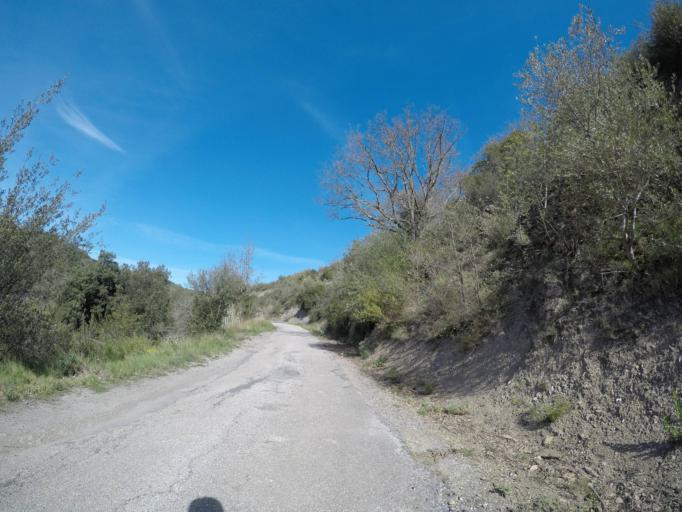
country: FR
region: Languedoc-Roussillon
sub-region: Departement des Pyrenees-Orientales
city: Thuir
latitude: 42.6286
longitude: 2.7044
